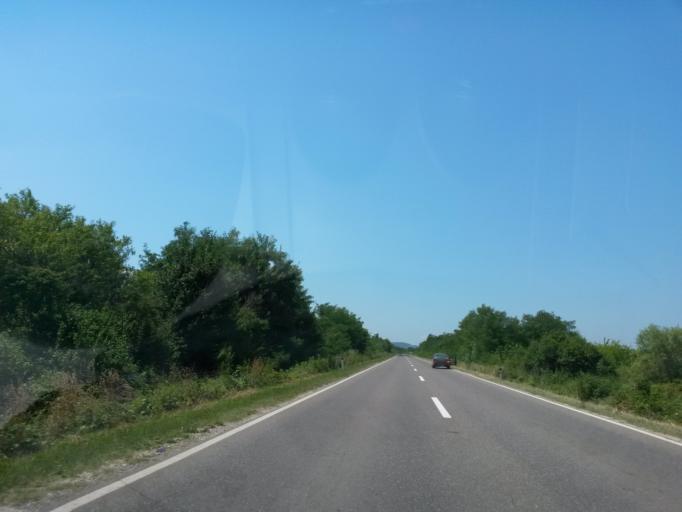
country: BA
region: Federation of Bosnia and Herzegovina
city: Odzak
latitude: 44.9788
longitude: 18.3637
